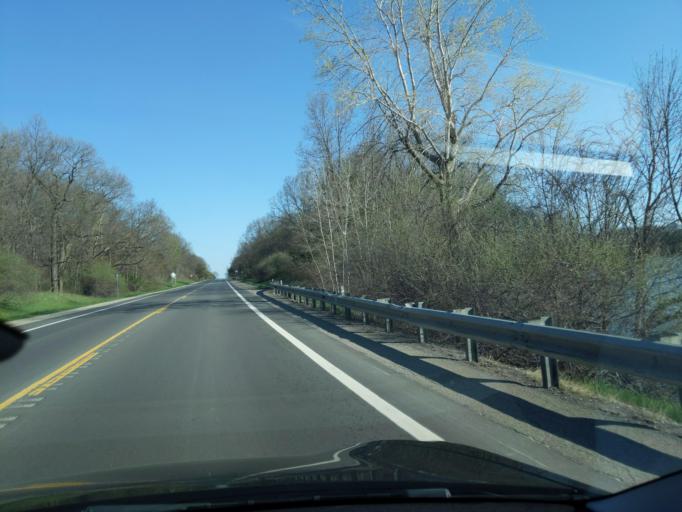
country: US
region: Michigan
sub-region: Washtenaw County
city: Chelsea
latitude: 42.3702
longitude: -84.0700
